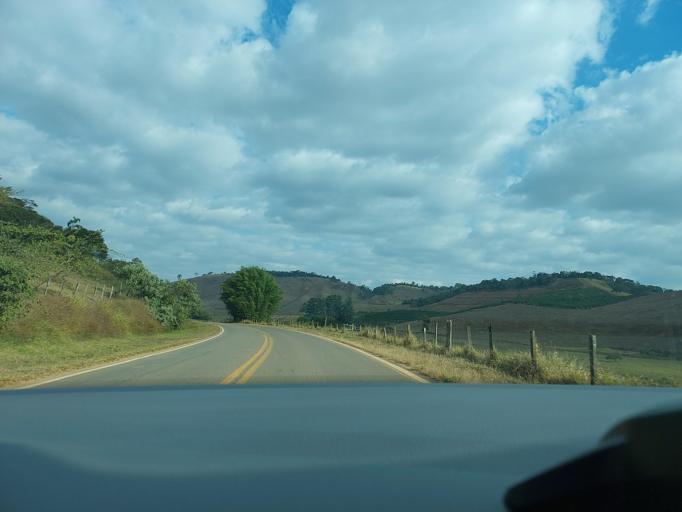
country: BR
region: Minas Gerais
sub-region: Visconde Do Rio Branco
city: Visconde do Rio Branco
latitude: -20.8656
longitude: -42.6715
